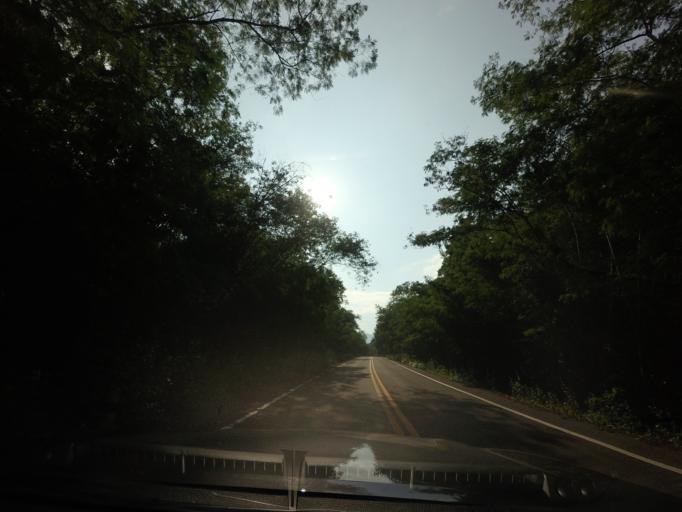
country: TH
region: Nan
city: Na Noi
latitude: 18.3639
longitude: 100.8725
